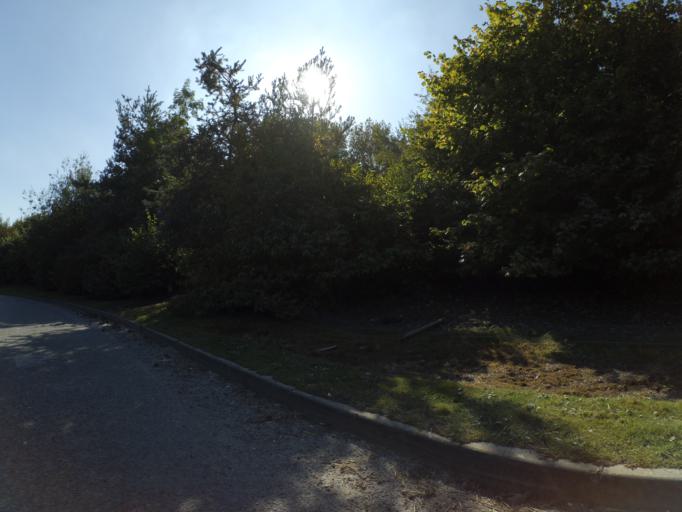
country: GB
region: England
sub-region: Warwickshire
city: Rugby
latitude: 52.4038
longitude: -1.2661
